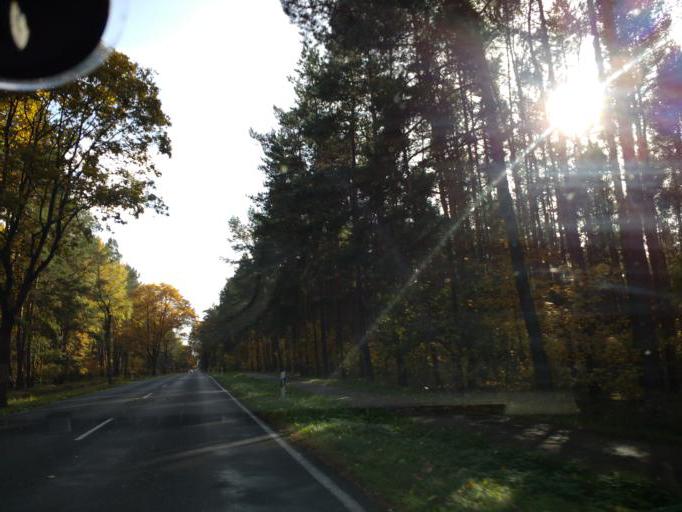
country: DE
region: Brandenburg
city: Grunheide
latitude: 52.3887
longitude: 13.8273
